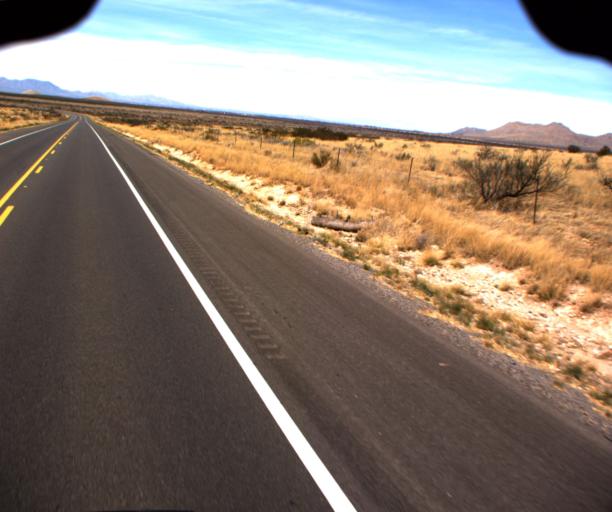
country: US
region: Arizona
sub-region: Cochise County
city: Willcox
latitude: 31.9026
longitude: -109.7134
